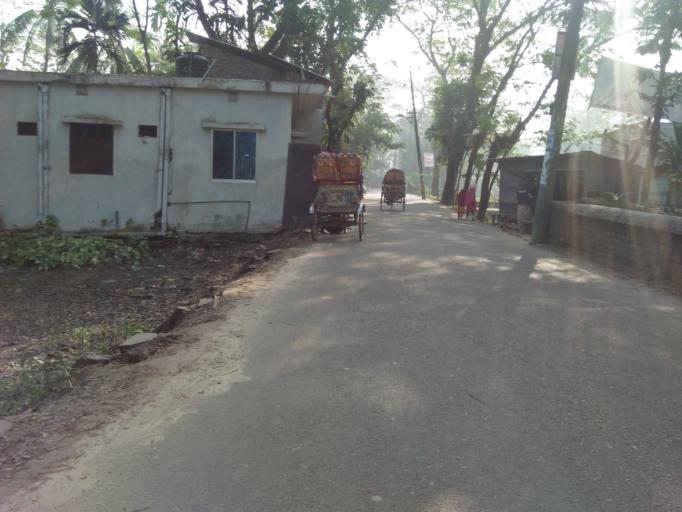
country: BD
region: Barisal
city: Bhola
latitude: 22.6795
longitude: 90.6402
